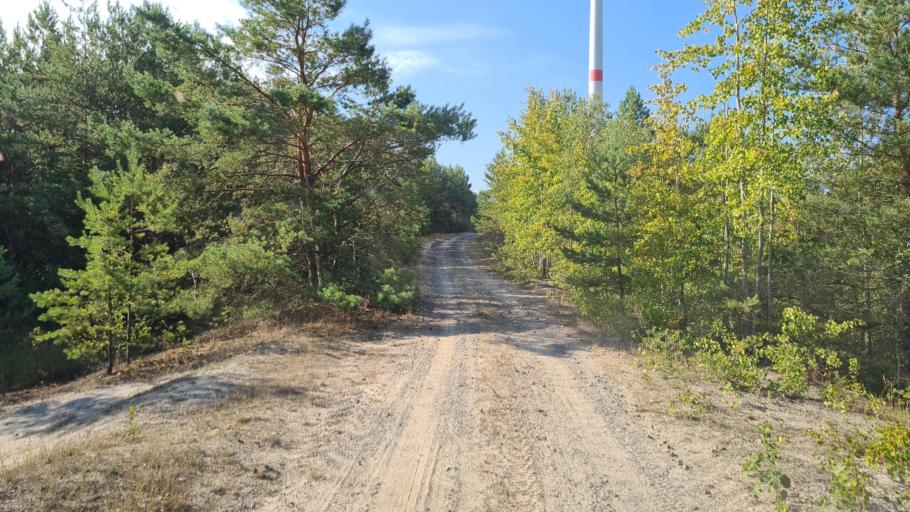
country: DE
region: Brandenburg
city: Sallgast
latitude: 51.5609
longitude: 13.8436
